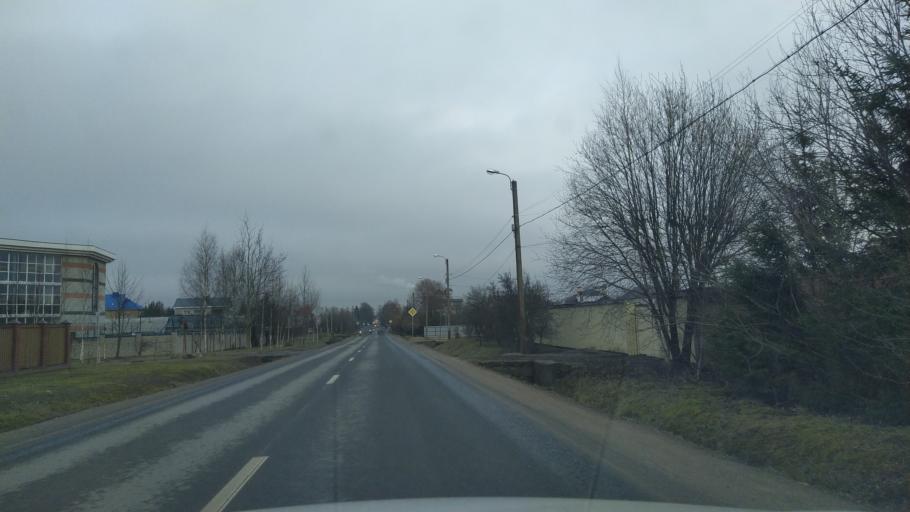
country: RU
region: St.-Petersburg
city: Aleksandrovskaya
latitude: 59.7231
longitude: 30.3474
